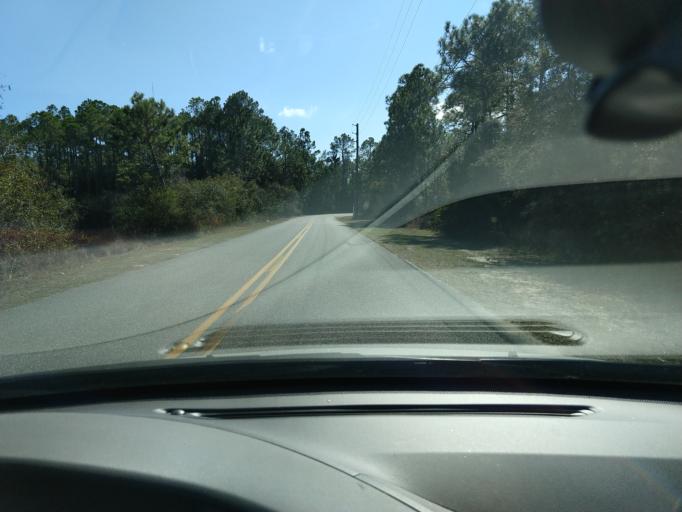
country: US
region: Florida
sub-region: Walton County
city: Miramar Beach
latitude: 30.3889
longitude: -86.3020
